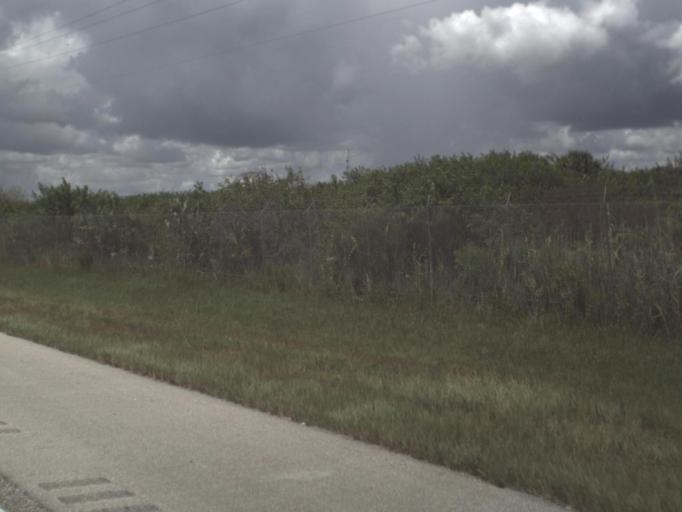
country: US
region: Florida
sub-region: Collier County
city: Immokalee
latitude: 26.1549
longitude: -81.3385
